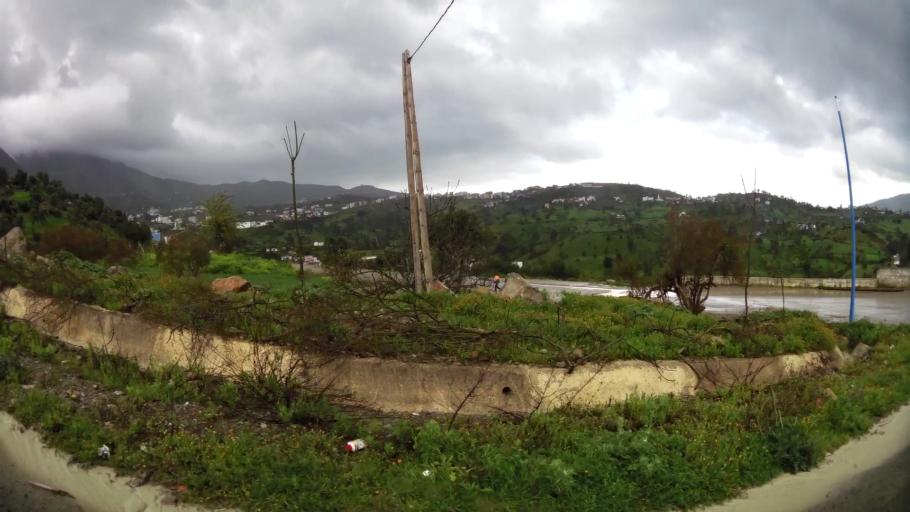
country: MA
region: Tanger-Tetouan
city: Chefchaouene
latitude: 35.1657
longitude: -5.2788
